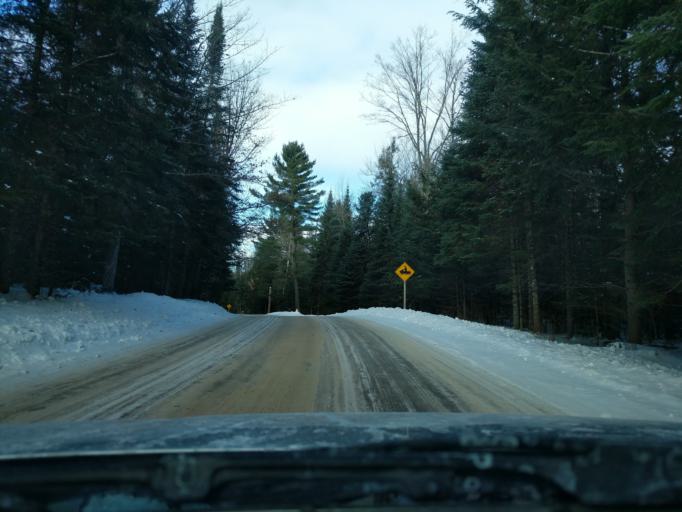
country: US
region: Wisconsin
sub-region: Vilas County
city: Eagle River
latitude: 45.8060
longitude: -89.0705
